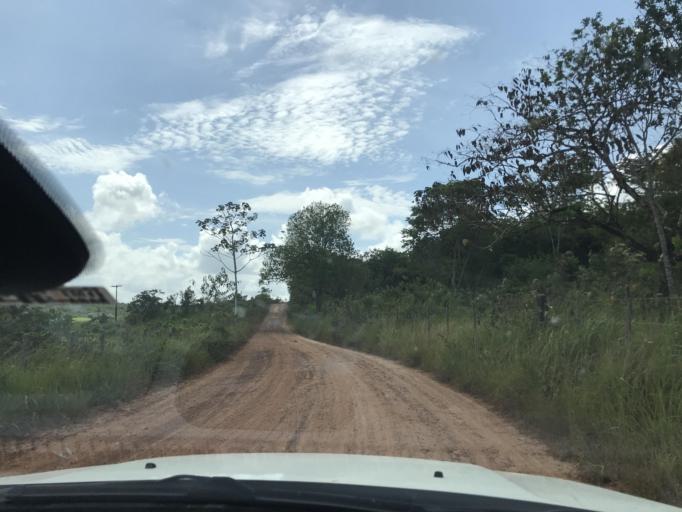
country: BR
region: Bahia
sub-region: Entre Rios
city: Entre Rios
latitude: -12.1783
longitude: -38.0619
